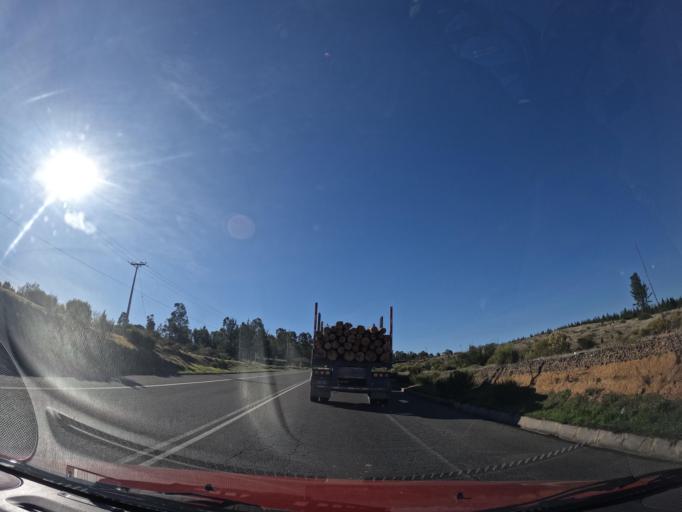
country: CL
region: Maule
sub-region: Provincia de Cauquenes
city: Cauquenes
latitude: -35.9333
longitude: -72.1943
